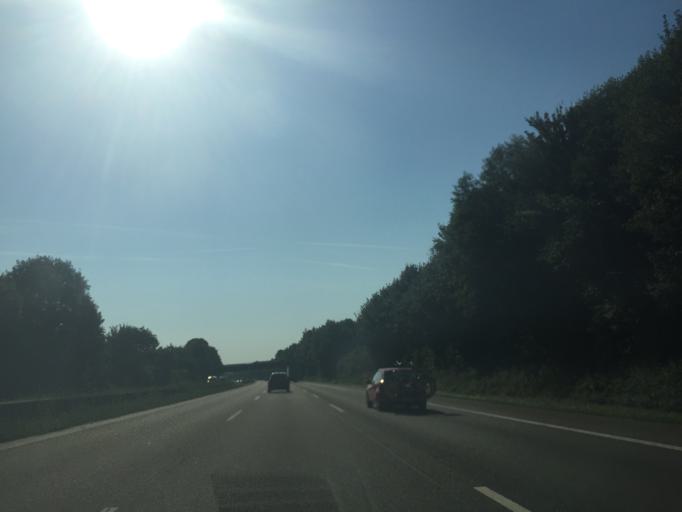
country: DE
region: Baden-Wuerttemberg
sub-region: Karlsruhe Region
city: Horrenberg
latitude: 49.2706
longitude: 8.7728
